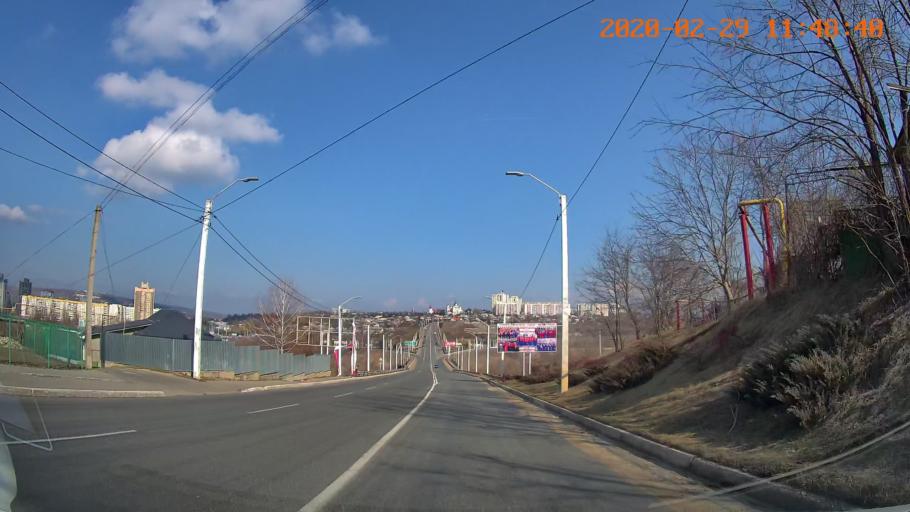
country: MD
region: Rezina
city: Rezina
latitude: 47.7494
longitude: 28.9918
